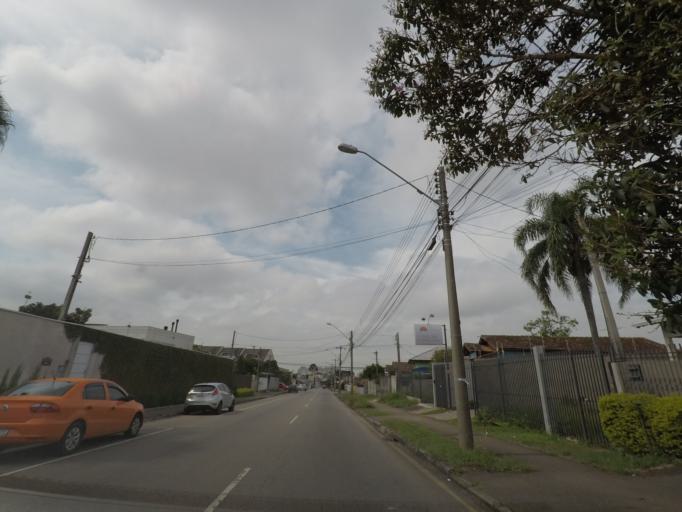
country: BR
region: Parana
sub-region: Curitiba
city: Curitiba
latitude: -25.4965
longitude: -49.2858
